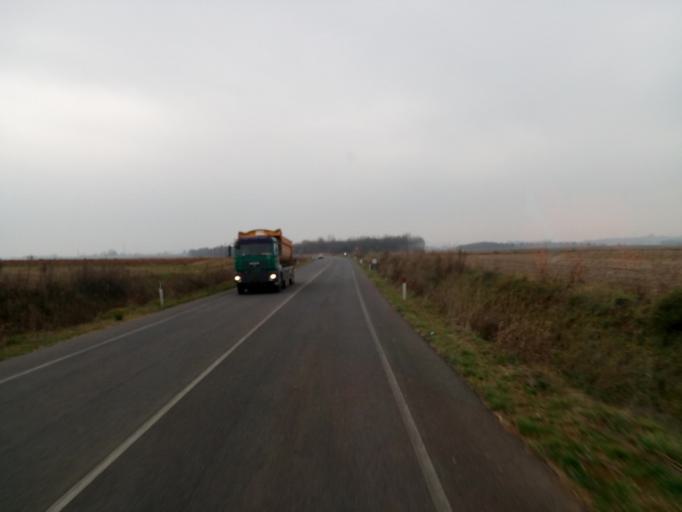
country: IT
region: Friuli Venezia Giulia
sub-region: Provincia di Udine
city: Orsaria
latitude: 46.0390
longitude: 13.3500
